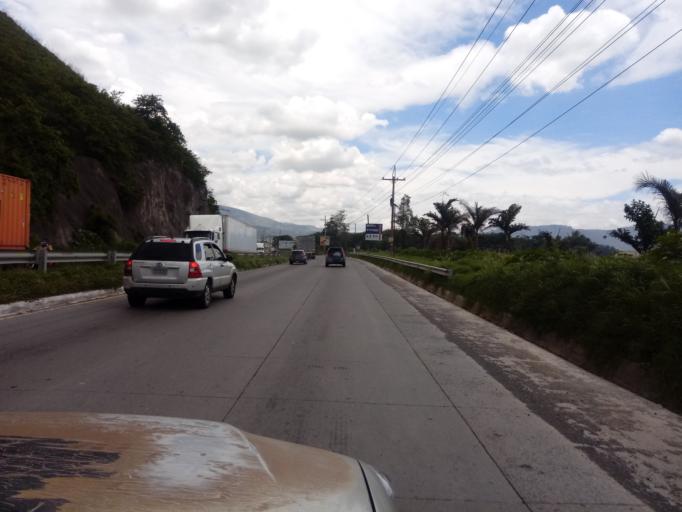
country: GT
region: Escuintla
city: San Vicente Pacaya
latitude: 14.4543
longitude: -90.6432
